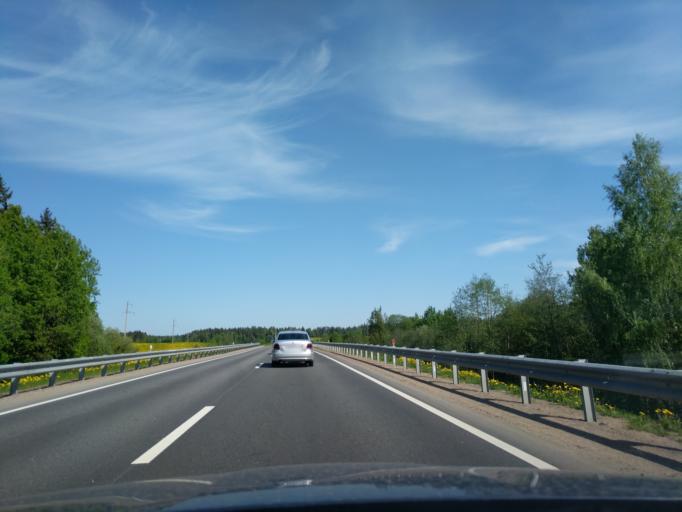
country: BY
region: Minsk
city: Bal'shavik
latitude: 54.0966
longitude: 27.5353
